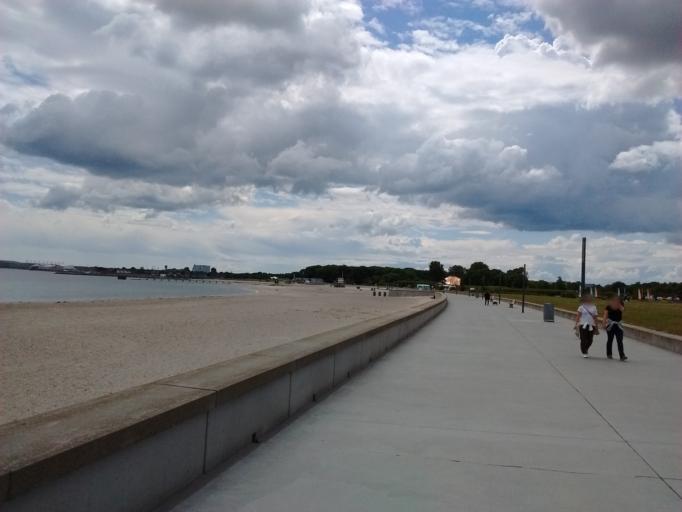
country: DK
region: Capital Region
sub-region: Tarnby Kommune
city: Tarnby
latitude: 55.6532
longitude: 12.6480
